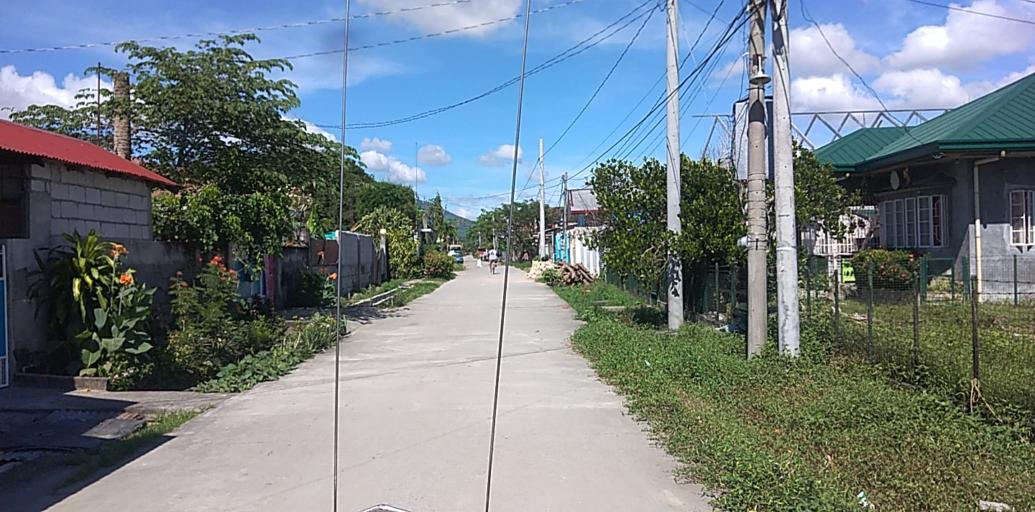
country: PH
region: Central Luzon
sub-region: Province of Pampanga
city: Arayat
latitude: 15.1336
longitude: 120.7755
